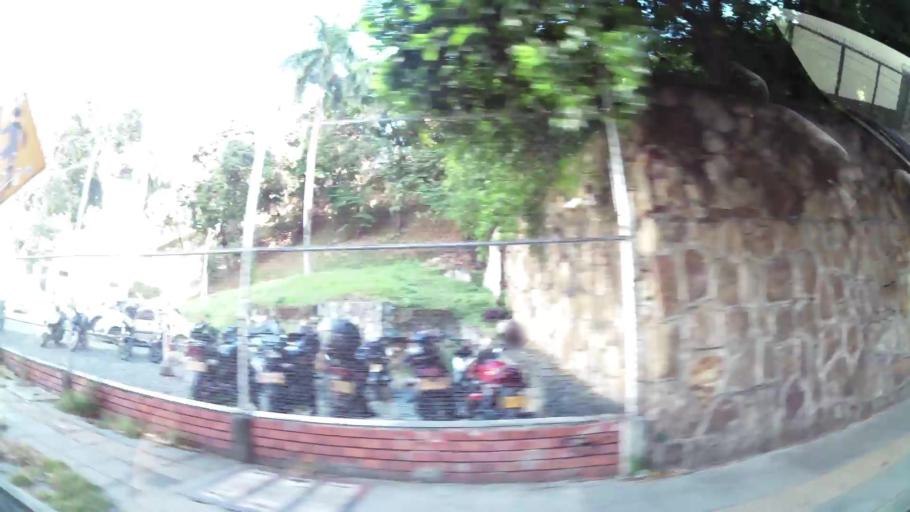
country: CO
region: Valle del Cauca
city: Cali
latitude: 3.4552
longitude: -76.5367
